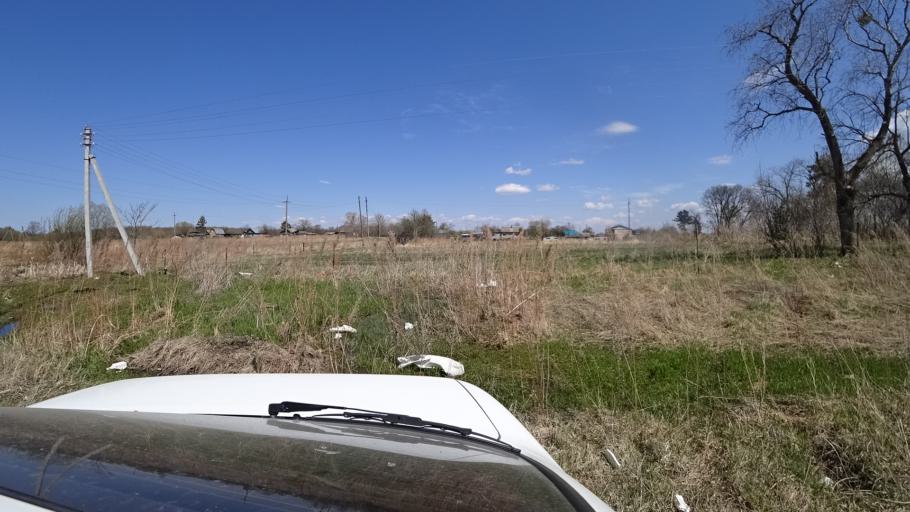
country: RU
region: Primorskiy
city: Lazo
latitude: 45.8025
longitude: 133.7621
